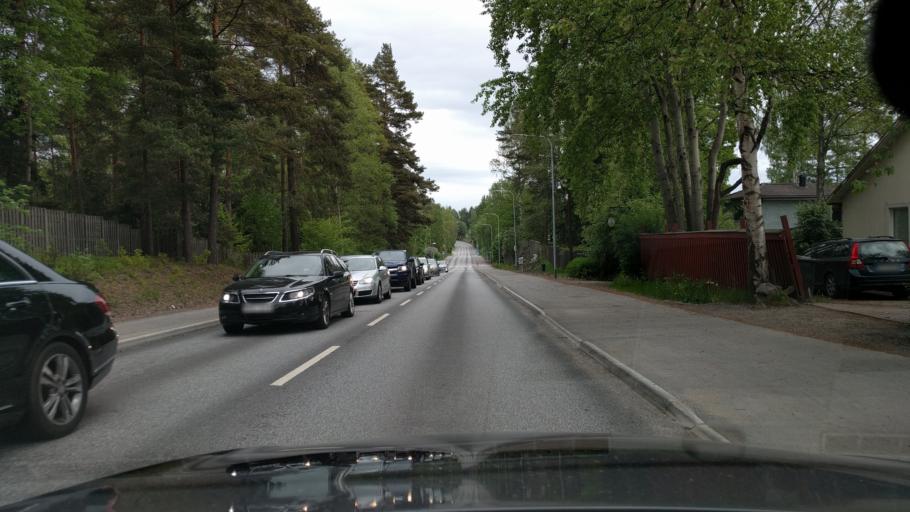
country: SE
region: Stockholm
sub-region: Taby Kommun
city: Taby
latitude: 59.4522
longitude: 18.0506
